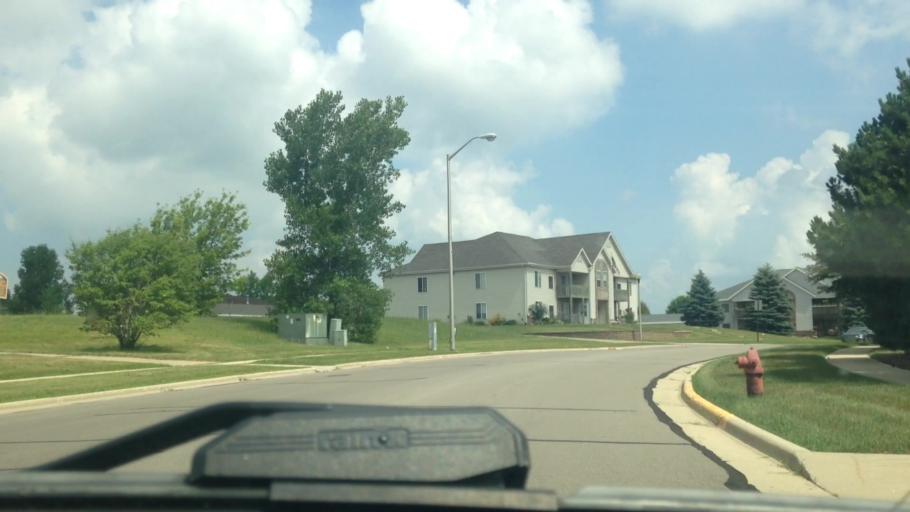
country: US
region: Wisconsin
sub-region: Dodge County
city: Mayville
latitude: 43.4951
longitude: -88.5675
